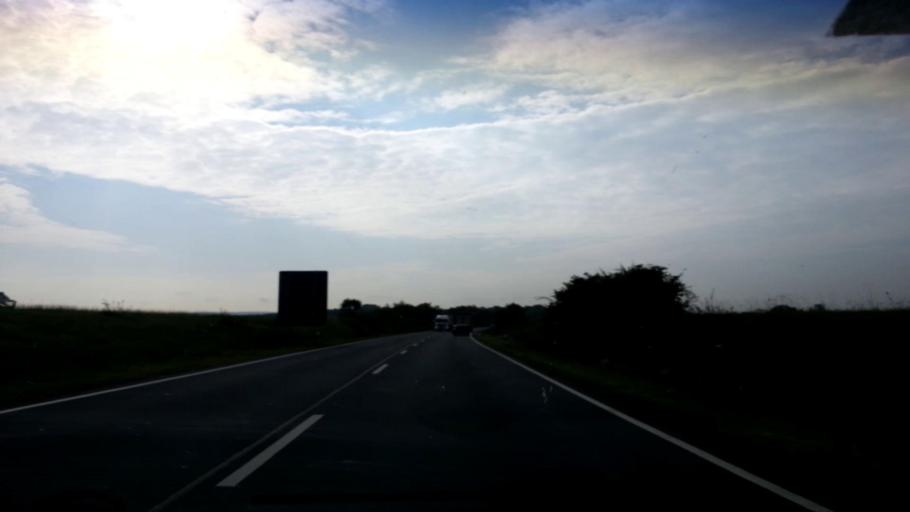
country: DE
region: Bavaria
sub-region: Regierungsbezirk Unterfranken
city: Prichsenstadt
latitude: 49.8413
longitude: 10.3520
